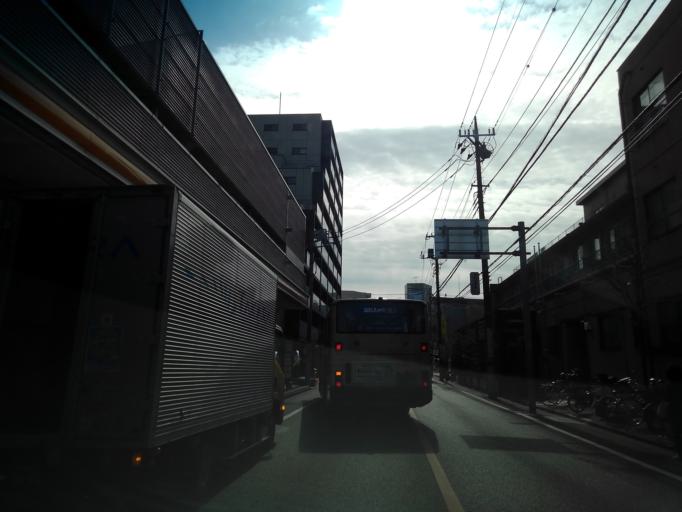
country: JP
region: Tokyo
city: Tanashicho
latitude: 35.7762
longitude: 139.5180
